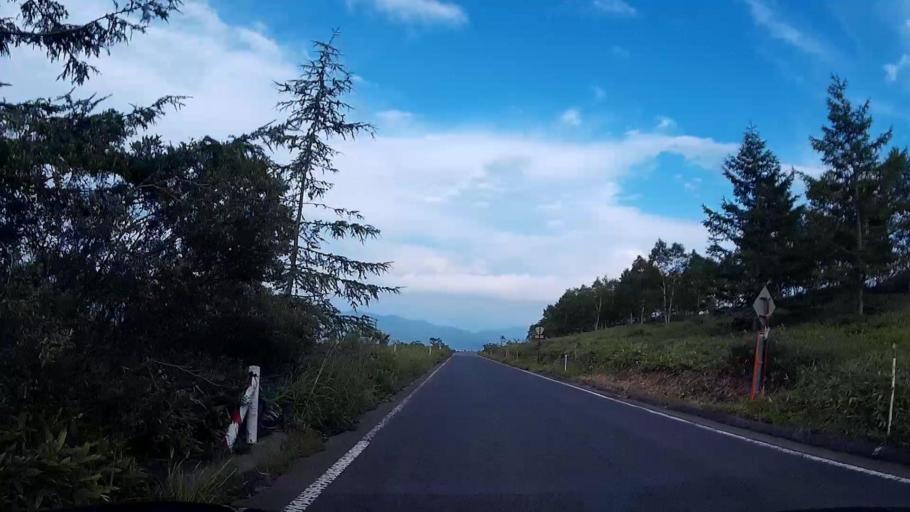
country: JP
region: Nagano
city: Nakano
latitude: 36.6330
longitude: 138.5508
